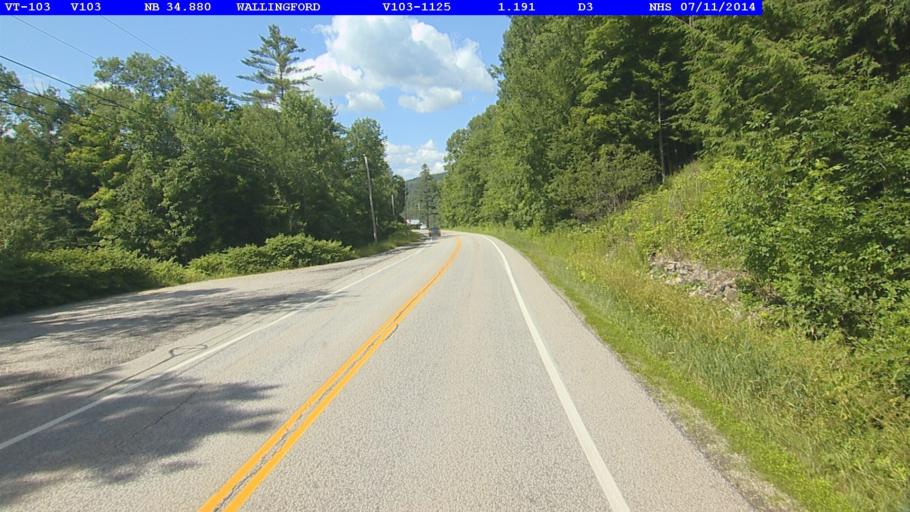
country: US
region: Vermont
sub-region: Rutland County
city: Rutland
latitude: 43.4669
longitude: -72.8751
